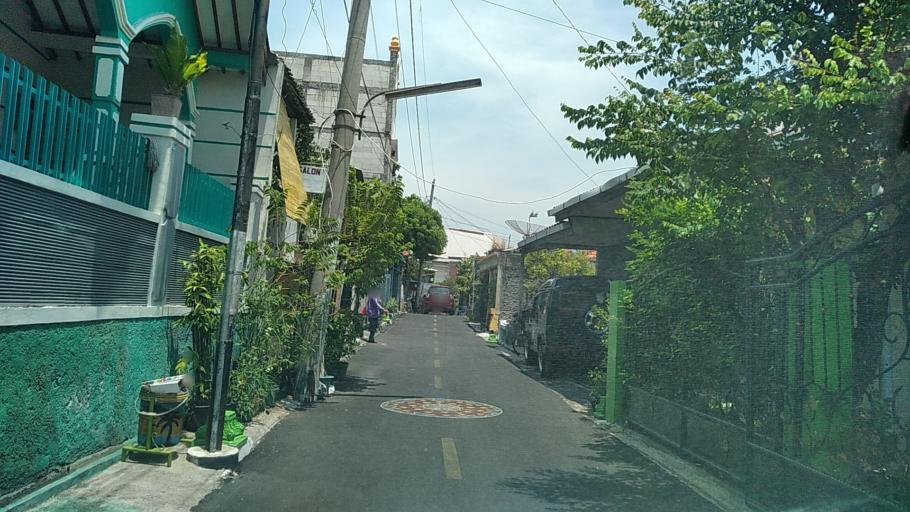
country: ID
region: Central Java
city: Semarang
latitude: -7.0118
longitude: 110.4465
